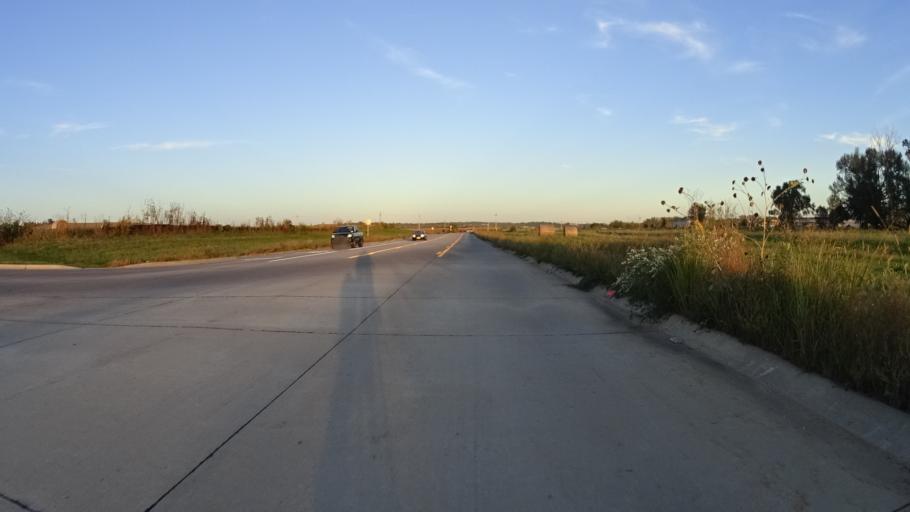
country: US
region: Nebraska
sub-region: Sarpy County
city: Offutt Air Force Base
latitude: 41.1451
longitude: -95.9710
